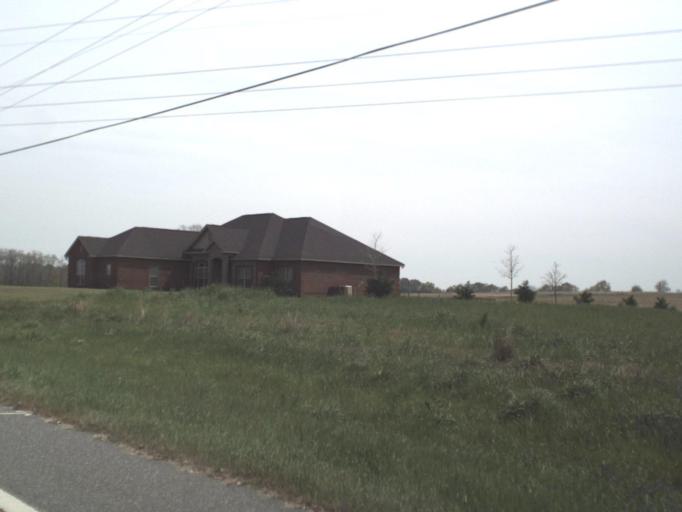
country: US
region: Florida
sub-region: Jackson County
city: Graceville
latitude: 30.9631
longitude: -85.5862
